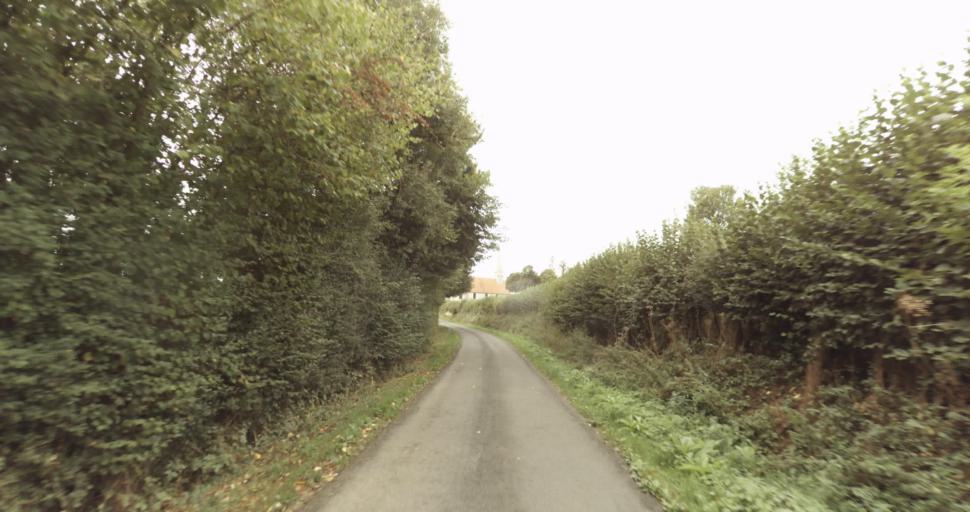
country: FR
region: Lower Normandy
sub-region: Departement de l'Orne
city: Gace
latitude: 48.8599
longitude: 0.2839
